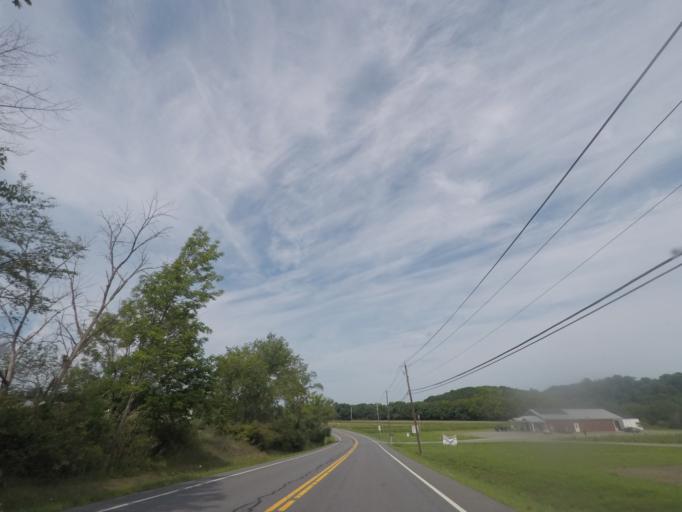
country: US
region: New York
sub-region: Rensselaer County
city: Wynantskill
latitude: 42.7308
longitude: -73.6138
